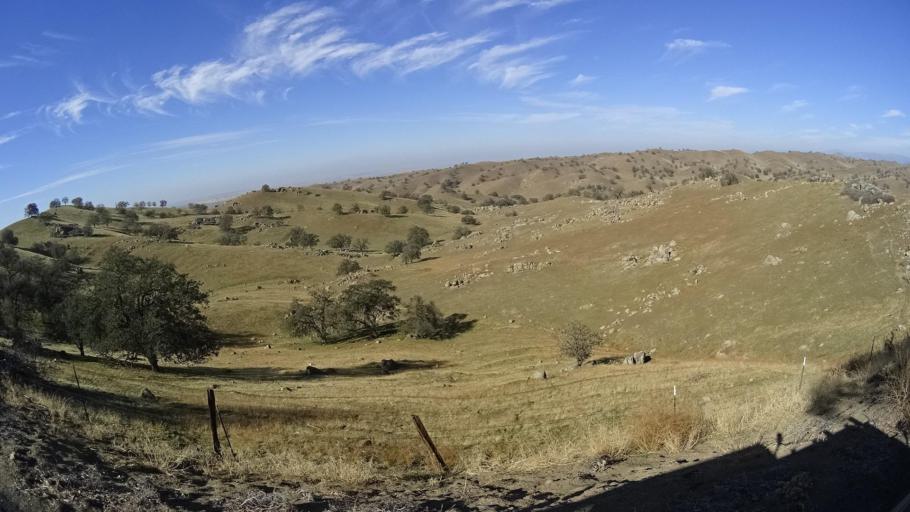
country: US
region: California
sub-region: Tulare County
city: Richgrove
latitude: 35.6941
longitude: -118.8639
